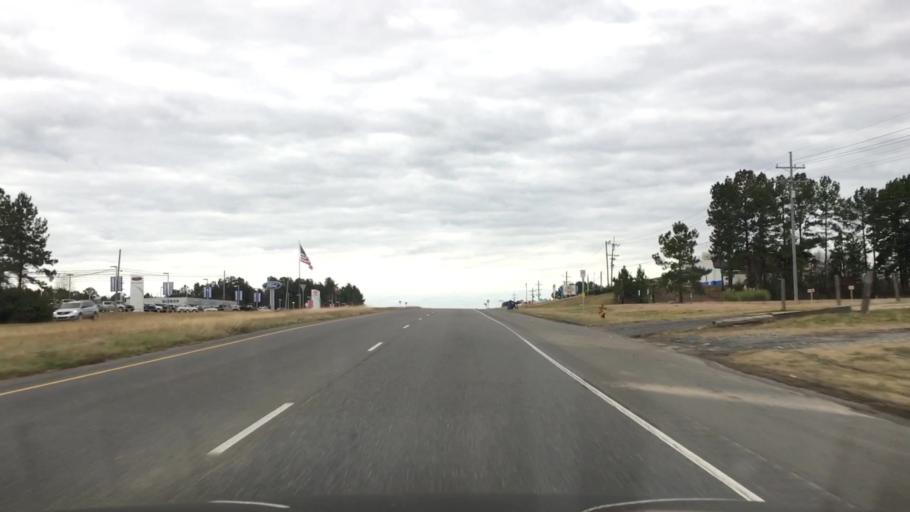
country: US
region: Louisiana
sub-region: Vernon Parish
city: New Llano
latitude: 31.0905
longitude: -93.2708
